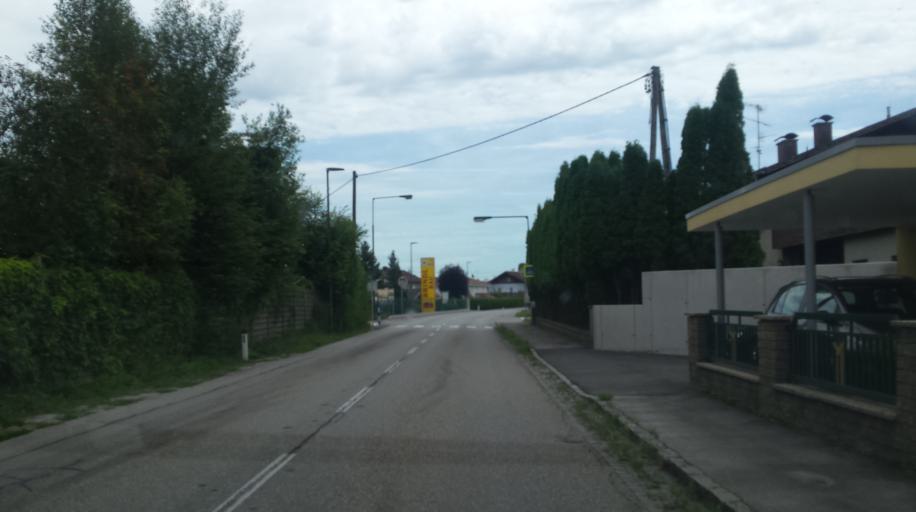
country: AT
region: Upper Austria
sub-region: Wels-Land
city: Bad Wimsbach-Neydharting
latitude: 48.0604
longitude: 13.9032
